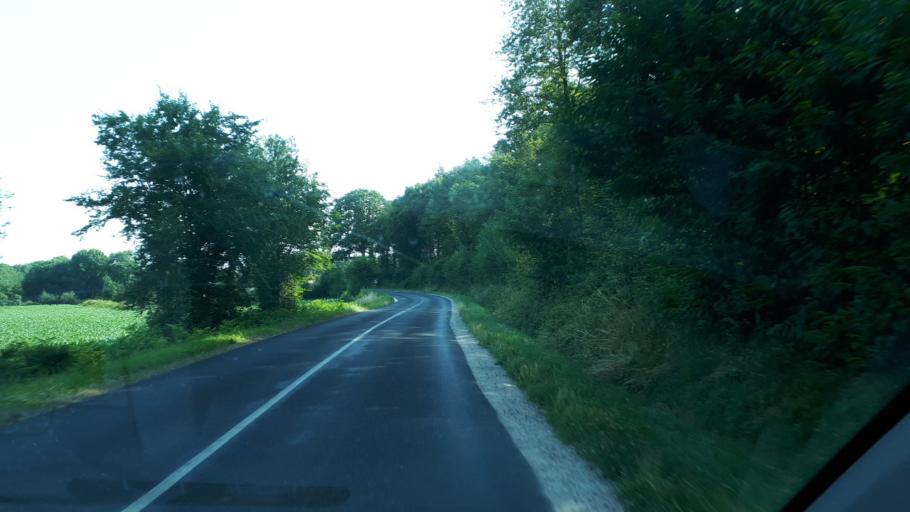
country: FR
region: Centre
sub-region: Departement du Loir-et-Cher
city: La Ville-aux-Clercs
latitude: 47.9299
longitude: 1.0851
